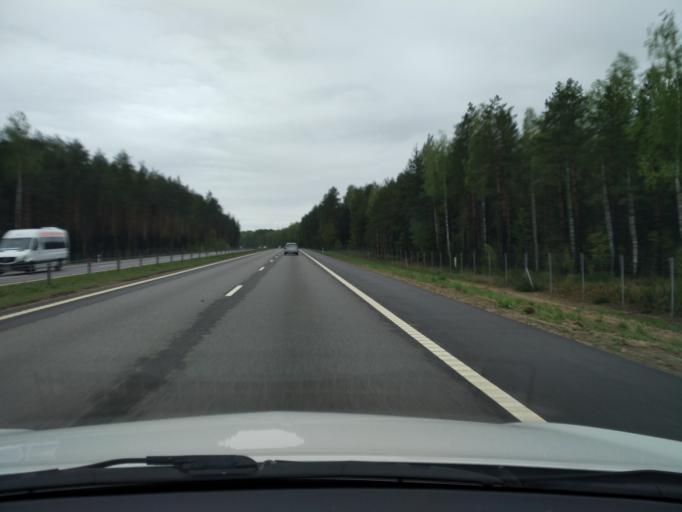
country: BY
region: Minsk
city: Pukhavichy
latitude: 53.4331
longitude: 28.4384
